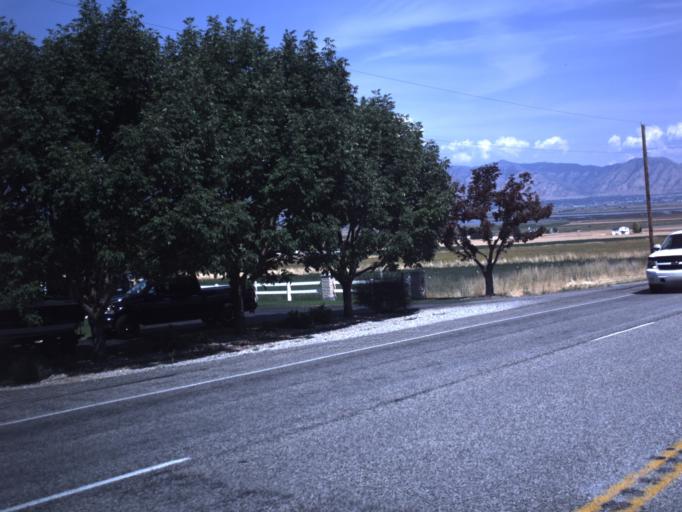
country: US
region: Utah
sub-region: Cache County
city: Mendon
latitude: 41.7554
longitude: -111.9989
